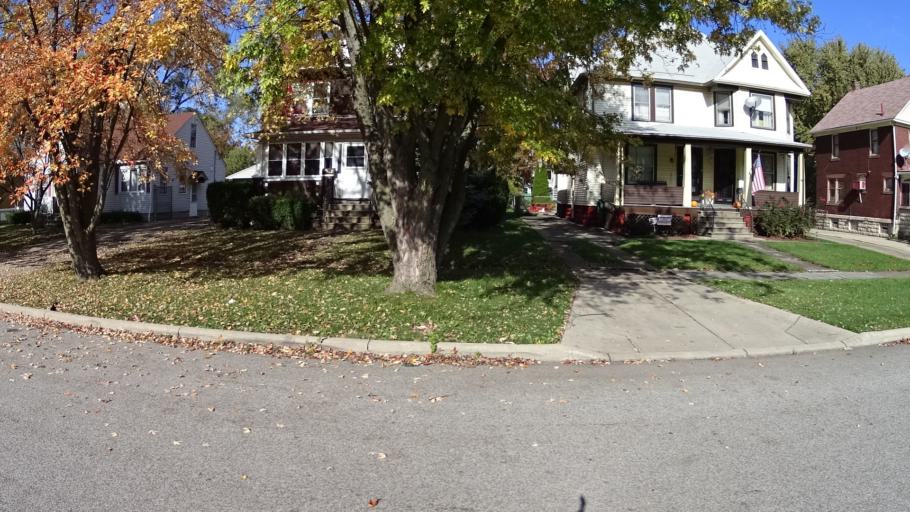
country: US
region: Ohio
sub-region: Lorain County
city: Sheffield
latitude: 41.4410
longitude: -82.1346
